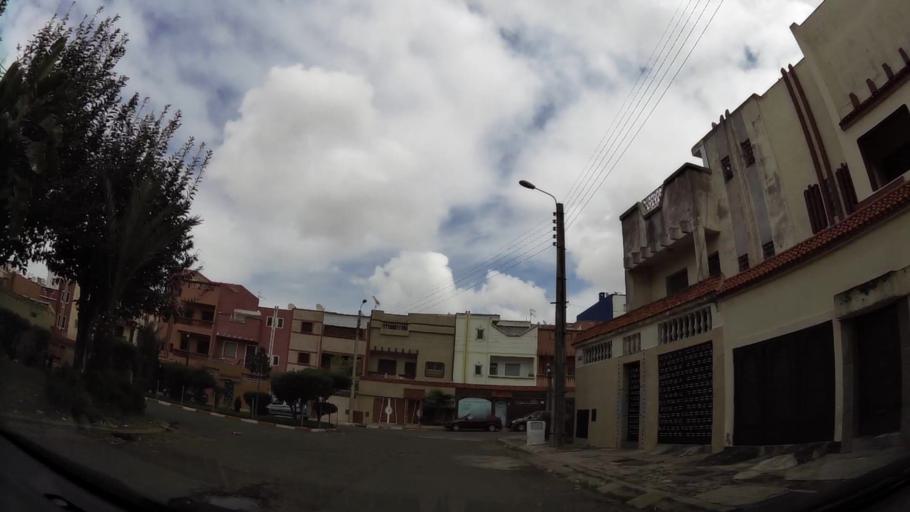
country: MA
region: Grand Casablanca
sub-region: Casablanca
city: Casablanca
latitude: 33.5368
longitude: -7.5985
